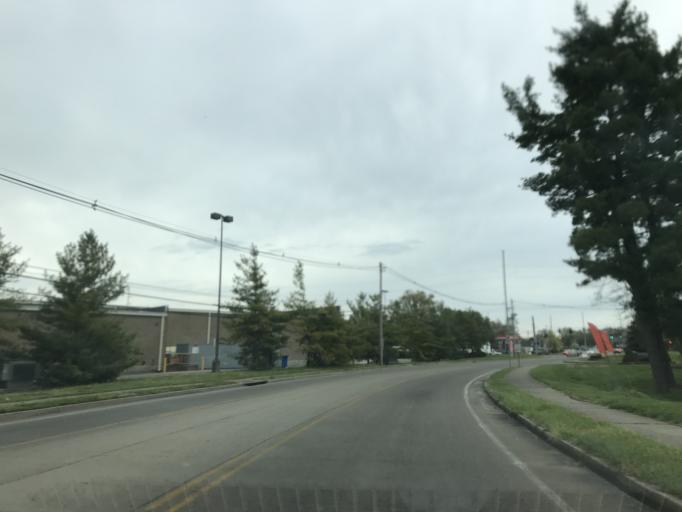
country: US
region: Kentucky
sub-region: Jefferson County
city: West Buechel
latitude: 38.1979
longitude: -85.6647
